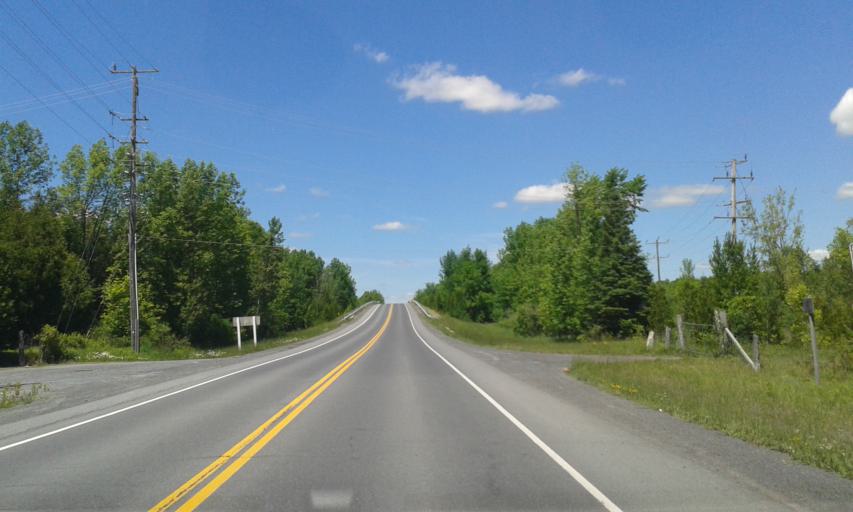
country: US
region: New York
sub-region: St. Lawrence County
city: Massena
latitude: 45.0385
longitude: -74.9034
